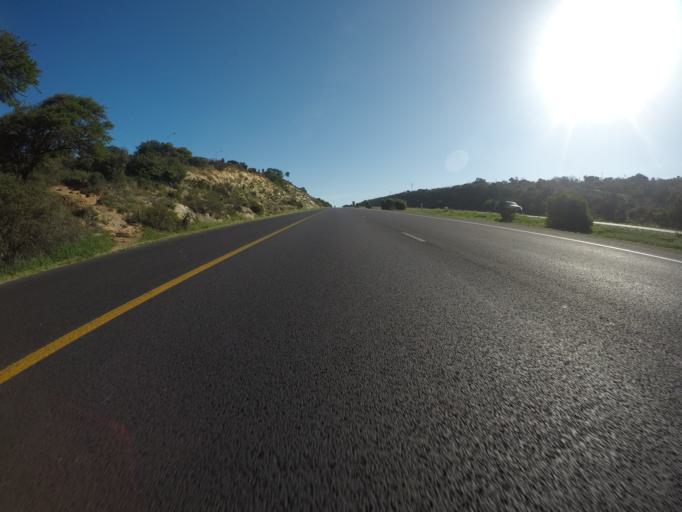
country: ZA
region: Western Cape
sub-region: Eden District Municipality
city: Mossel Bay
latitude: -34.1613
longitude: 22.0959
